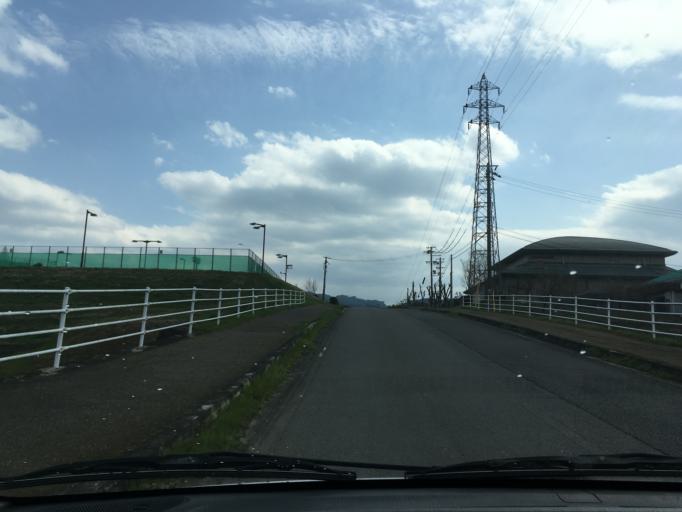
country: JP
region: Nara
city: Kashihara-shi
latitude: 34.4518
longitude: 135.7905
